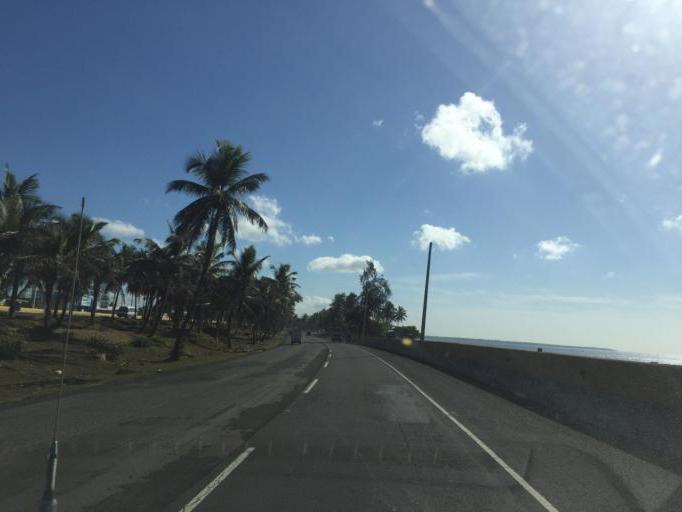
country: DO
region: Santo Domingo
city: Guerra
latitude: 18.4613
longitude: -69.7336
